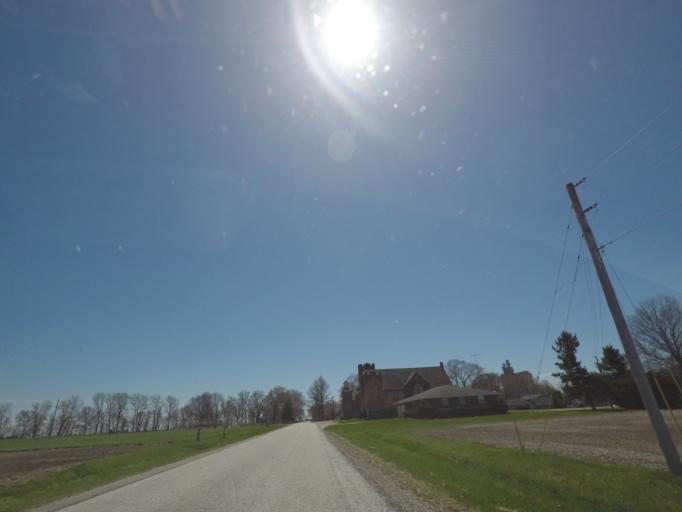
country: US
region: Illinois
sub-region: Logan County
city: Mount Pulaski
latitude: 40.0567
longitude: -89.1825
